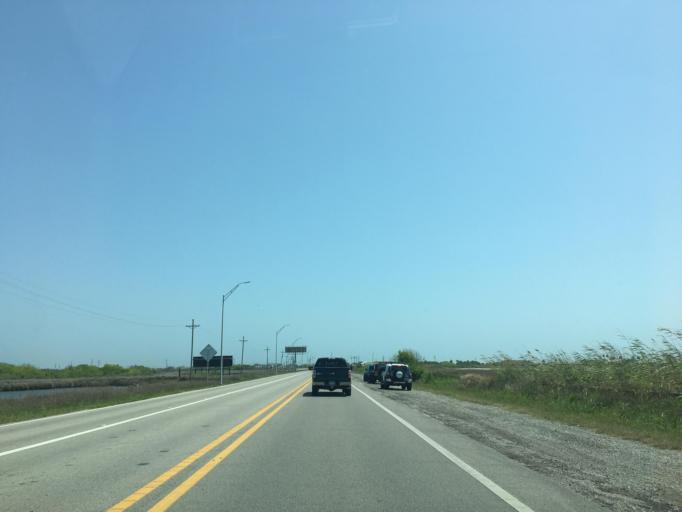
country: US
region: Texas
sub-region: Galveston County
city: Galveston
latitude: 29.3657
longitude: -94.7675
